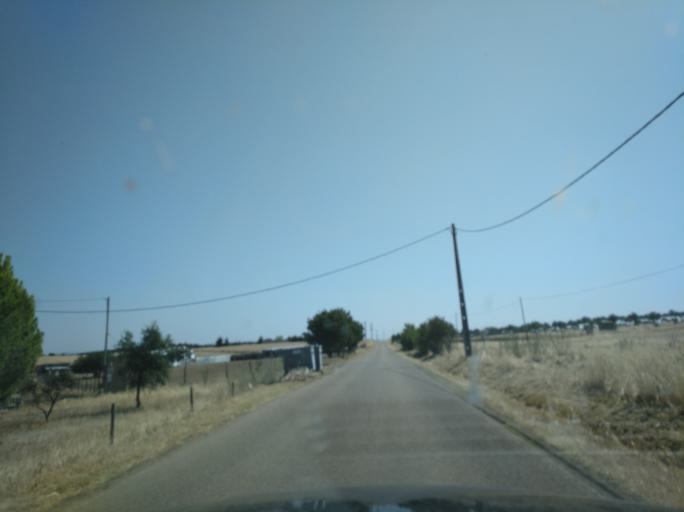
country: PT
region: Portalegre
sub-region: Campo Maior
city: Campo Maior
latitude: 39.0240
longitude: -7.0413
